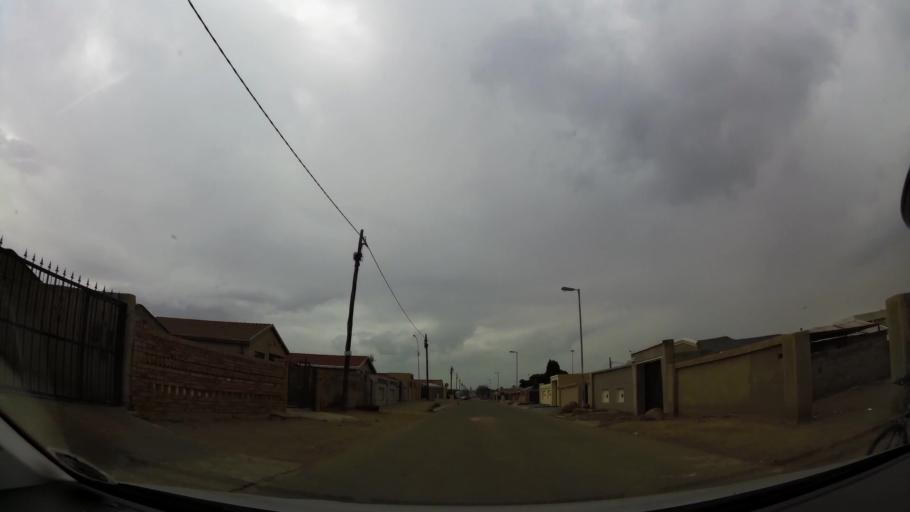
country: ZA
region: Gauteng
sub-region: City of Johannesburg Metropolitan Municipality
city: Soweto
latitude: -26.2601
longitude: 27.8651
